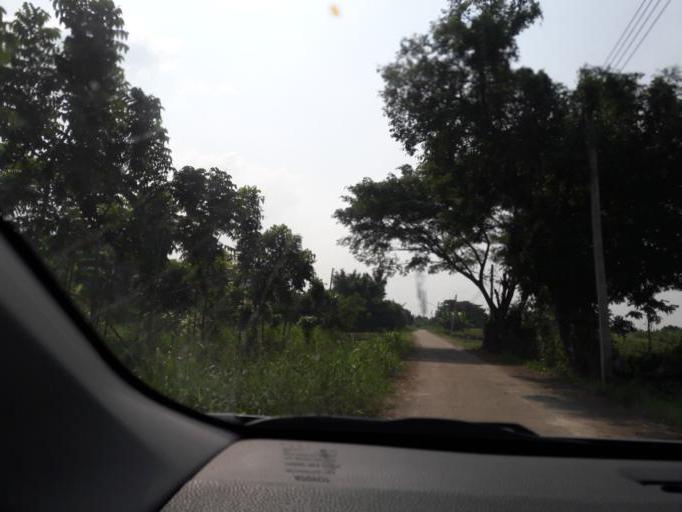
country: TH
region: Ang Thong
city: Ang Thong
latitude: 14.5475
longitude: 100.4393
